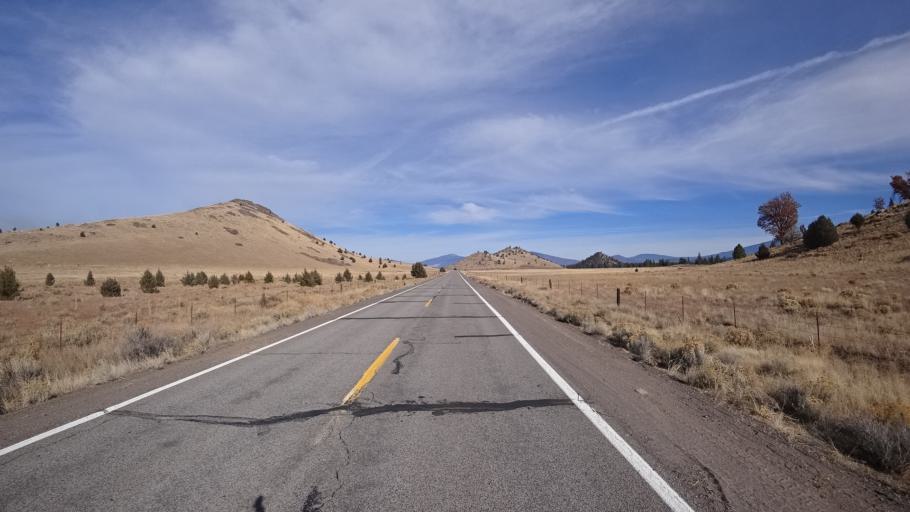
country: US
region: California
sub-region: Siskiyou County
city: Weed
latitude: 41.4889
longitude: -122.4066
